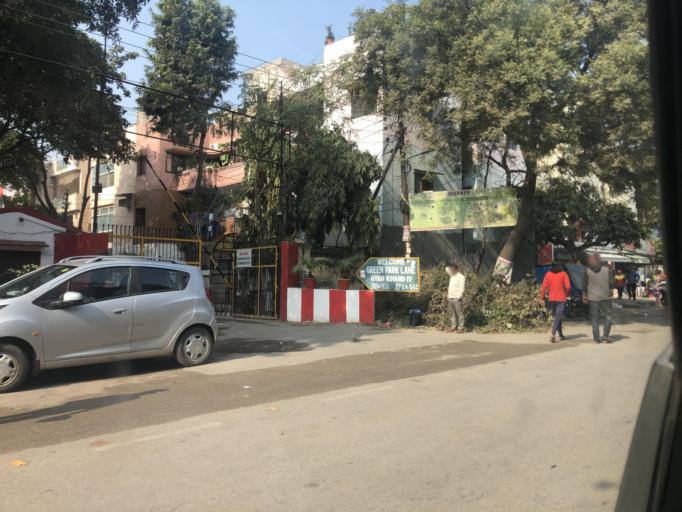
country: IN
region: Uttar Pradesh
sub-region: Gautam Buddha Nagar
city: Noida
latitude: 28.6448
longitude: 77.3598
